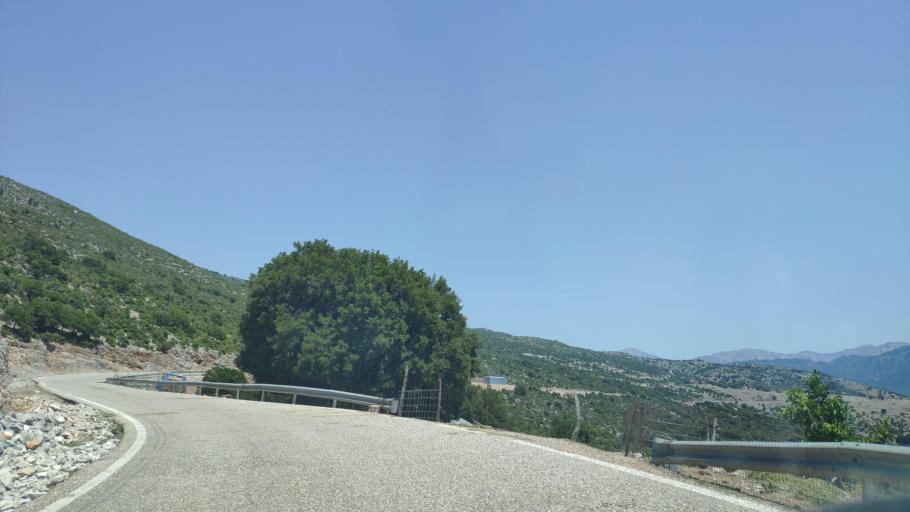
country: GR
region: West Greece
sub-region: Nomos Aitolias kai Akarnanias
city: Krikellos
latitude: 39.0637
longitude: 21.3824
